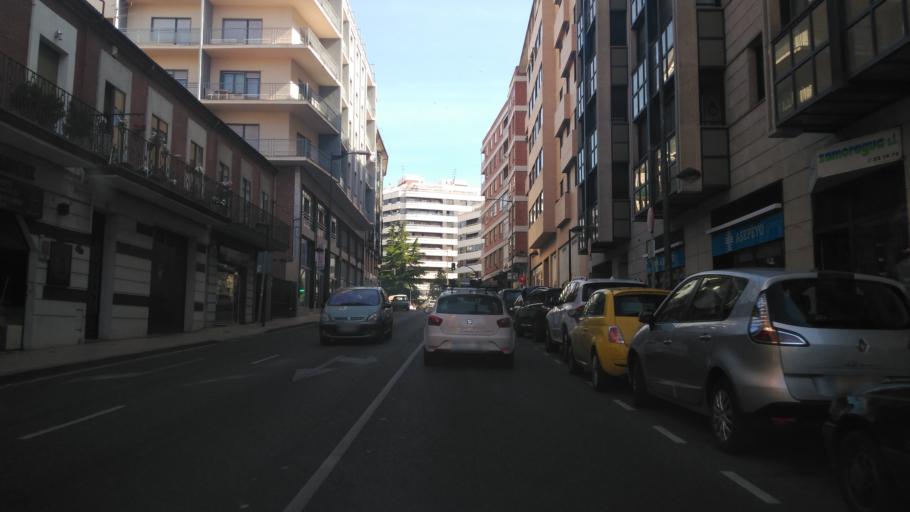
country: ES
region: Castille and Leon
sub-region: Provincia de Zamora
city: Zamora
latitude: 41.5049
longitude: -5.7399
